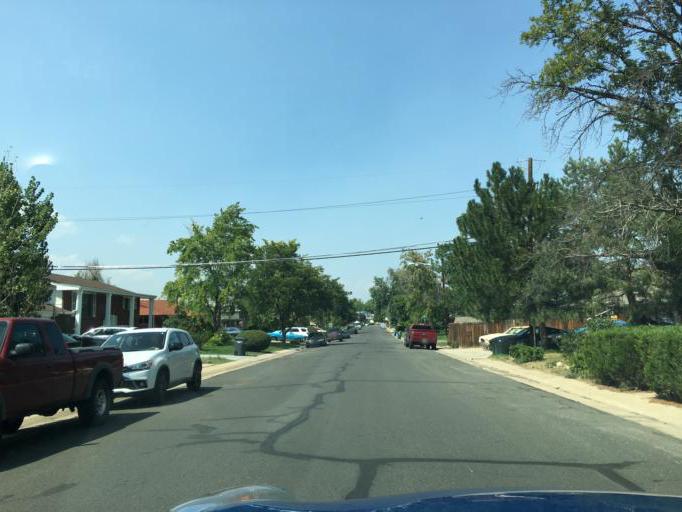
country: US
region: Colorado
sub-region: Adams County
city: Westminster
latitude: 39.8457
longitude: -105.0480
